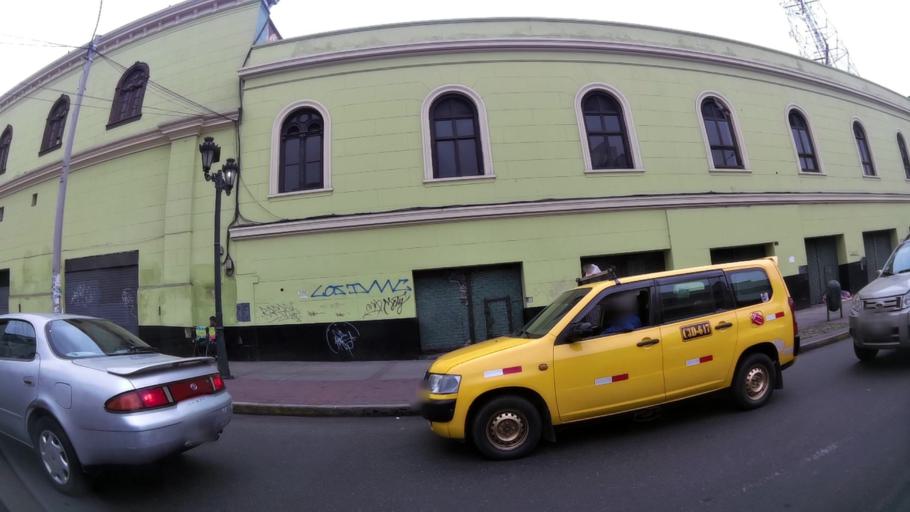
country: PE
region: Lima
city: Lima
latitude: -12.0560
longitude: -77.0388
